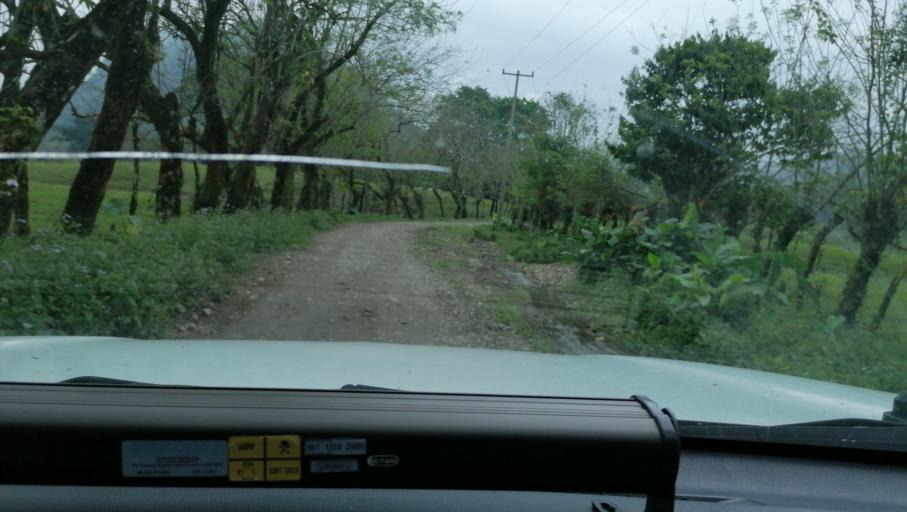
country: MX
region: Chiapas
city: Ixtacomitan
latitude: 17.3629
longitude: -93.1727
